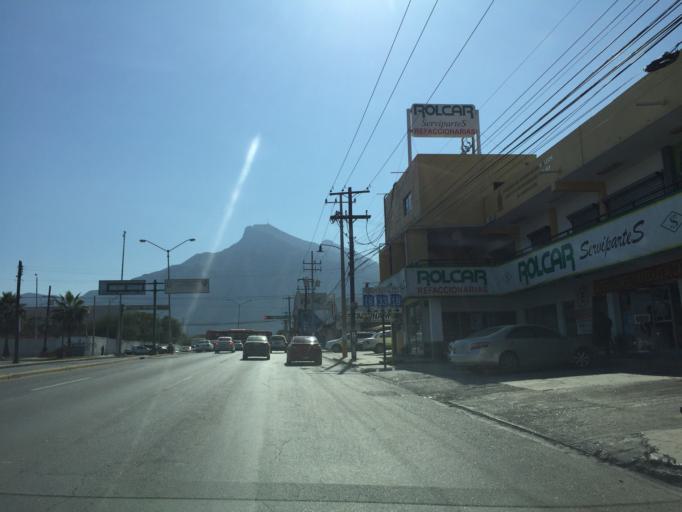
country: MX
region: Nuevo Leon
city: Guadalupe
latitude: 25.6838
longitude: -100.2305
